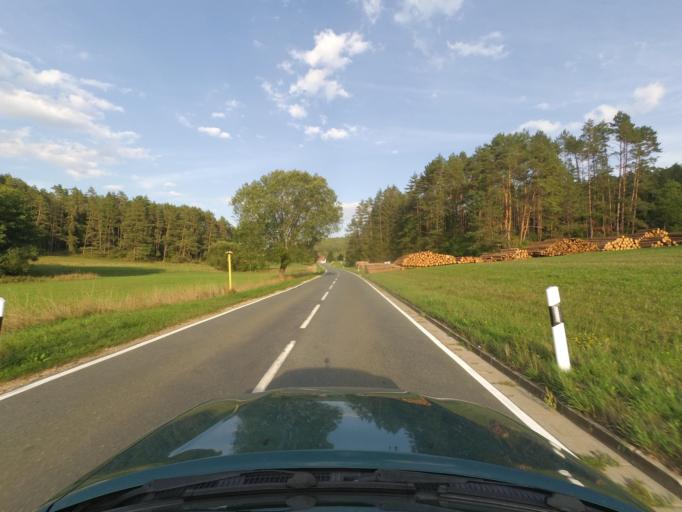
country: DE
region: Bavaria
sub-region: Upper Palatinate
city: Konigstein
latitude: 49.5747
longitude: 11.6031
